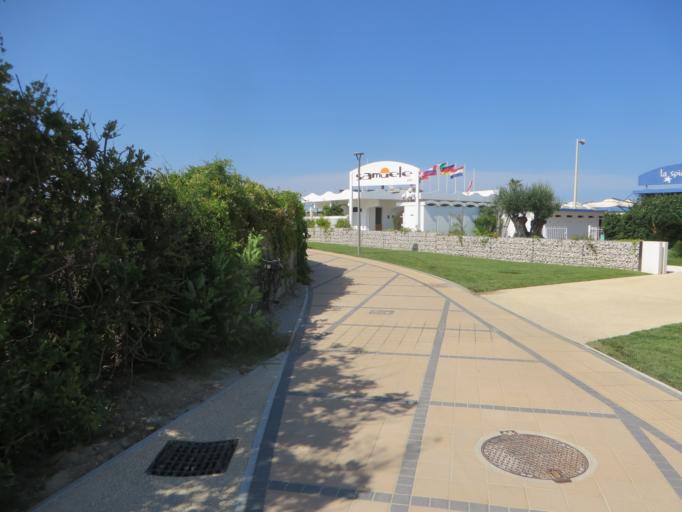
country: IT
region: Emilia-Romagna
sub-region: Provincia di Ravenna
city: Cervia
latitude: 44.2792
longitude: 12.3525
